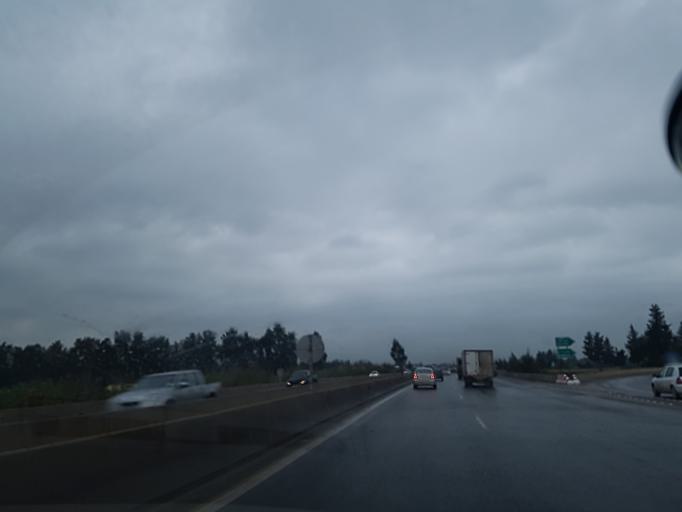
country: DZ
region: Boumerdes
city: Khemis el Khechna
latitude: 36.6700
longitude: 3.2897
